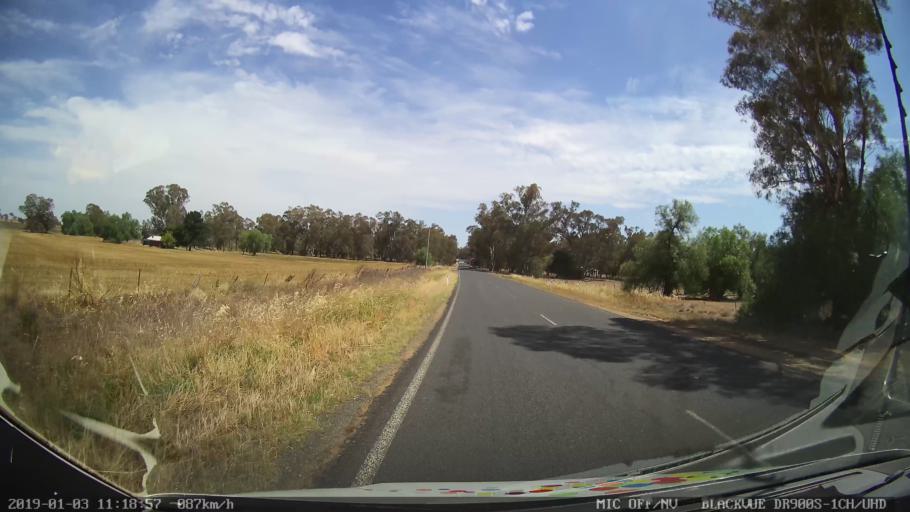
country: AU
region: New South Wales
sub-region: Young
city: Young
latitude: -34.1192
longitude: 148.2604
